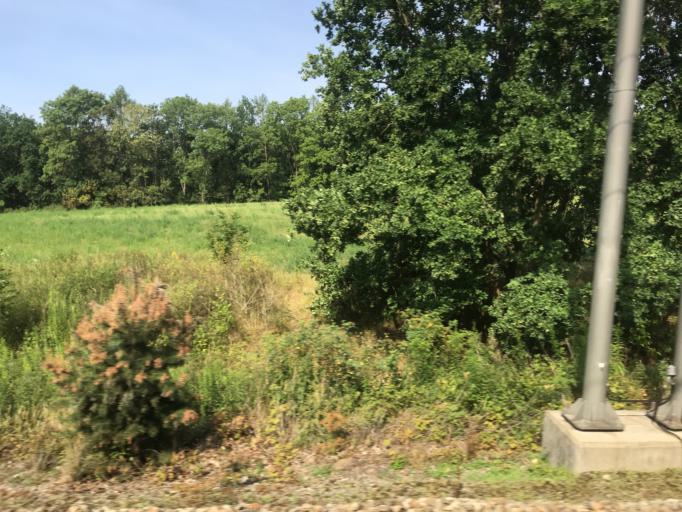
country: CZ
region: Central Bohemia
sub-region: Okres Praha-Vychod
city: Mnichovice
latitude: 49.9028
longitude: 14.7280
